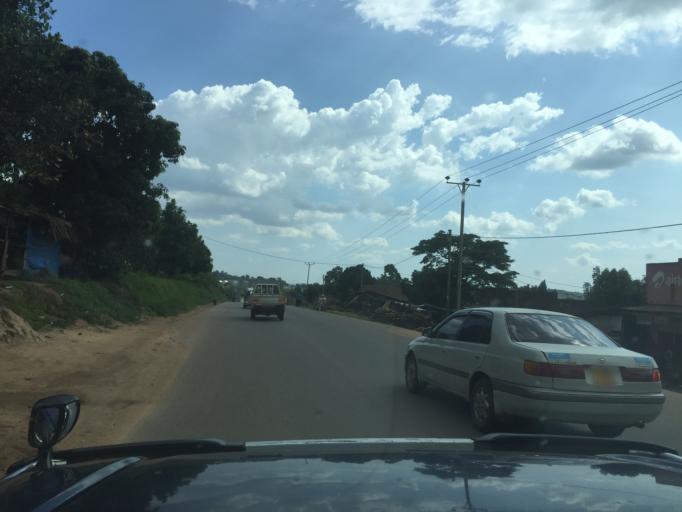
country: UG
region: Central Region
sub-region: Wakiso District
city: Wakiso
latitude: 0.5195
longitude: 32.5272
